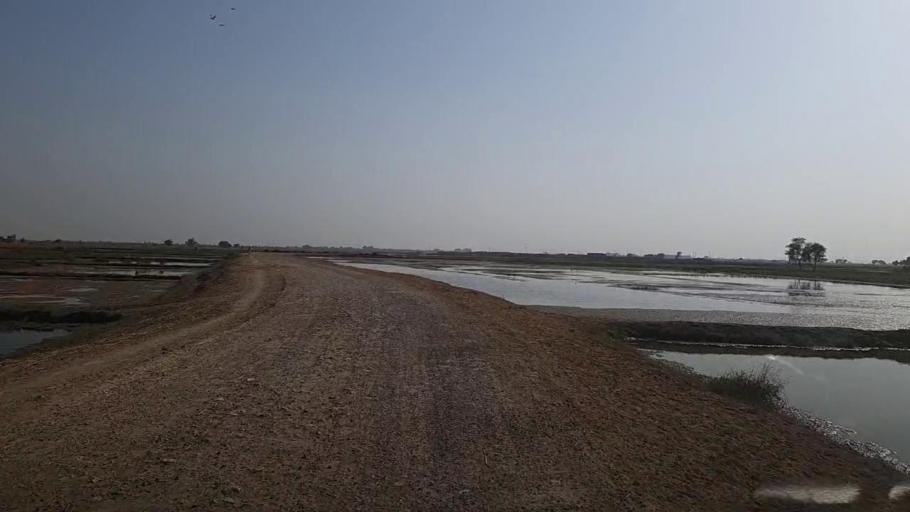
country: PK
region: Sindh
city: Kandhkot
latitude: 28.3747
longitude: 69.3330
